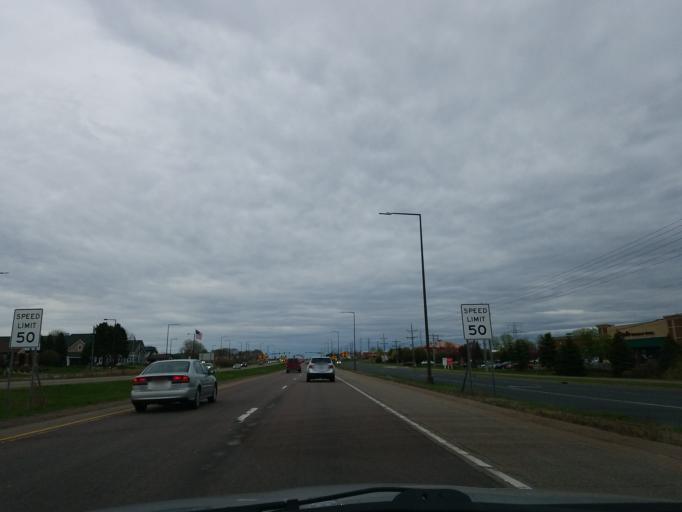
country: US
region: Minnesota
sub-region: Washington County
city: Stillwater
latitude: 45.0361
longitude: -92.8383
